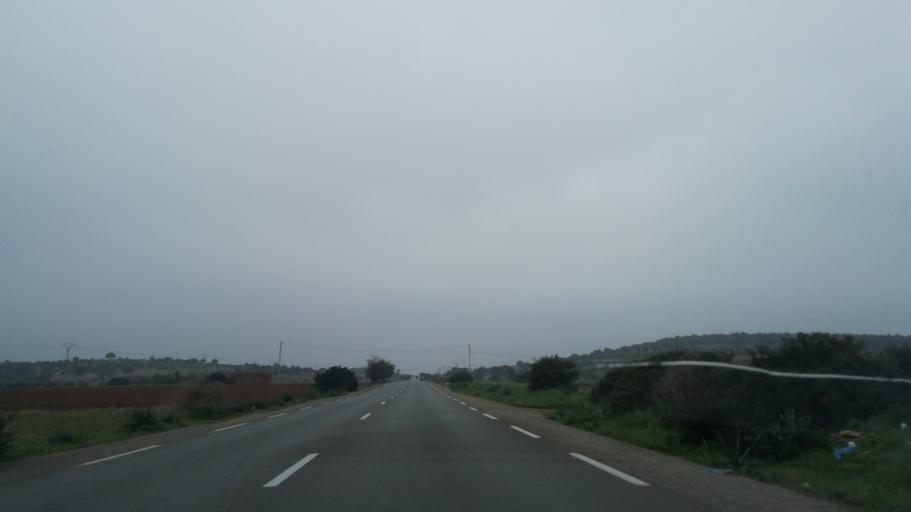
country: DZ
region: Mascara
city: Oued el Abtal
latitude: 35.2967
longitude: 0.4544
